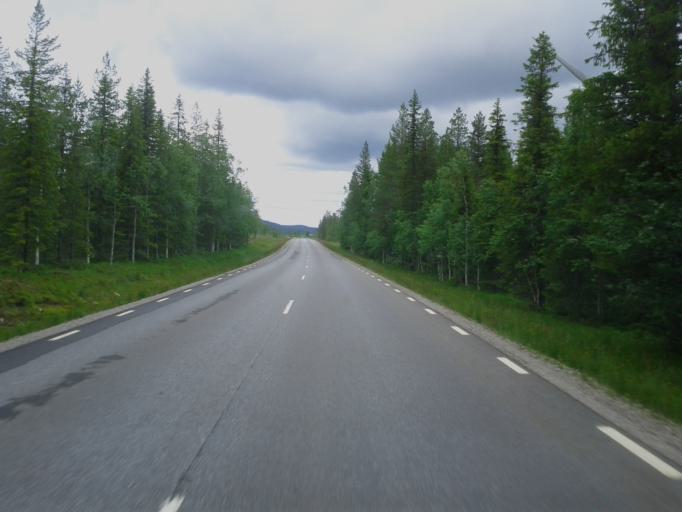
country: SE
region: Vaesterbotten
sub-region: Mala Kommun
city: Mala
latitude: 65.0672
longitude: 19.0351
